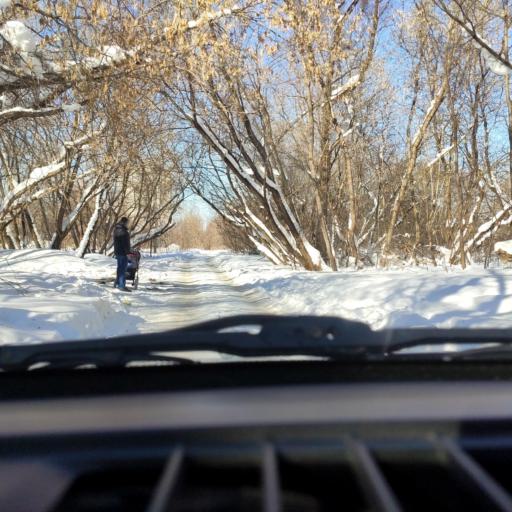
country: RU
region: Perm
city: Perm
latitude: 58.0656
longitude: 56.3597
